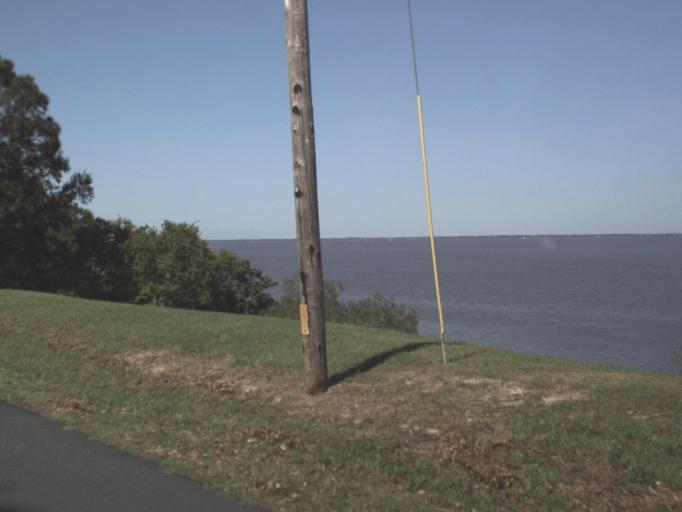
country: US
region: Florida
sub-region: Escambia County
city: East Pensacola Heights
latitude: 30.4417
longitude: -87.1737
